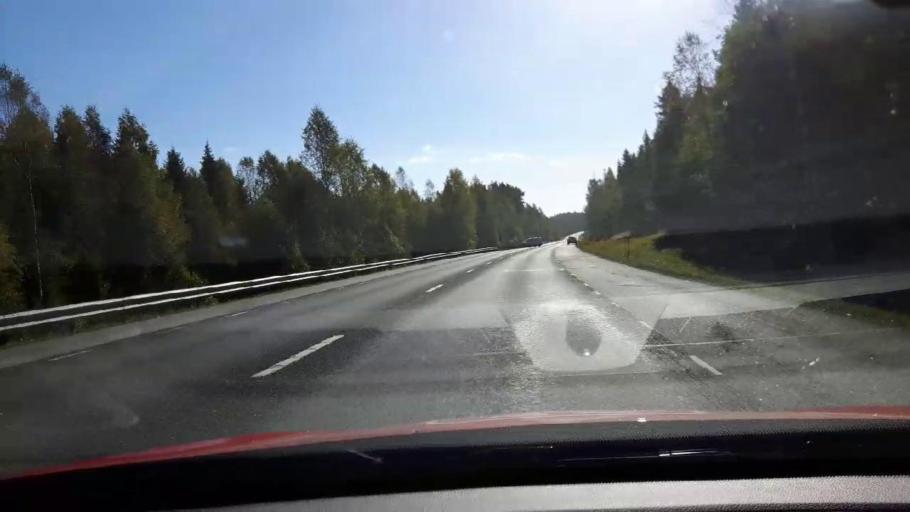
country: SE
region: Jaemtland
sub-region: Braecke Kommun
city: Braecke
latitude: 62.6994
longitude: 15.5202
